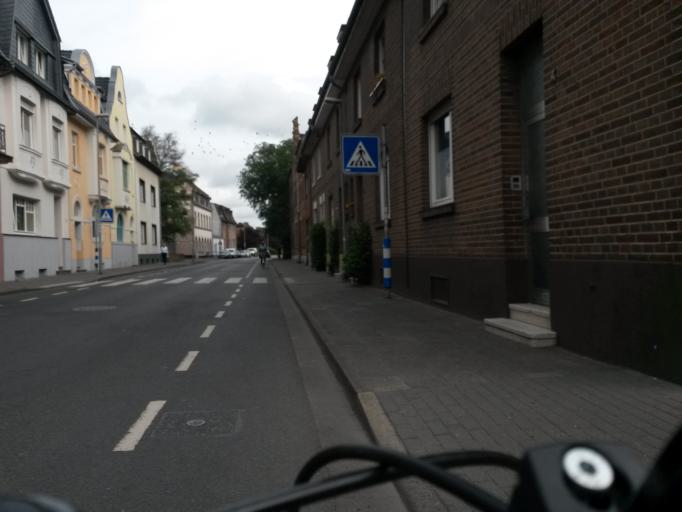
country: DE
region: North Rhine-Westphalia
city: Kempen
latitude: 51.3684
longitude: 6.4238
